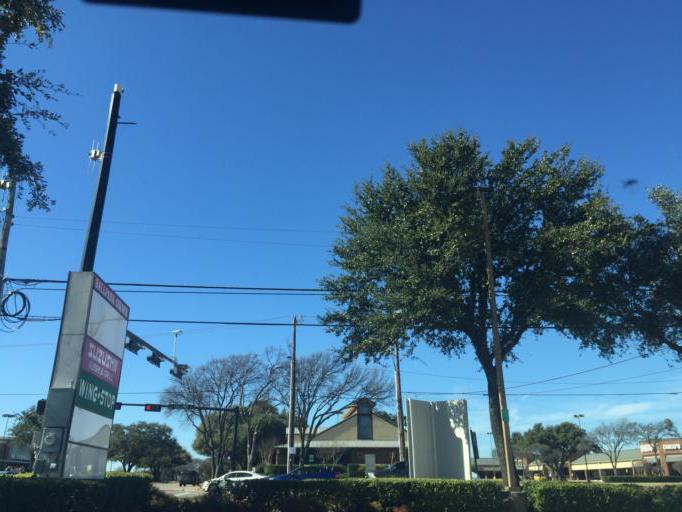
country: US
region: Texas
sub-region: Tarrant County
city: Arlington
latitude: 32.7557
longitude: -97.0968
